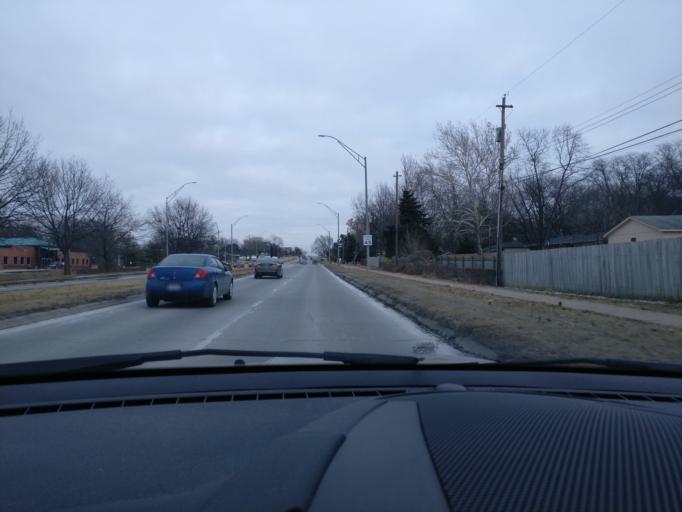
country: US
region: Nebraska
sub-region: Lancaster County
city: Lincoln
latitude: 40.8134
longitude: -96.6150
